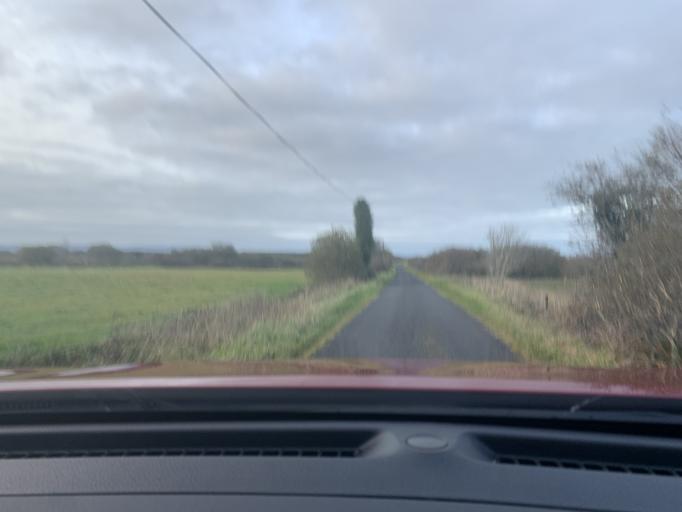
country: IE
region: Connaught
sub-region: Roscommon
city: Ballaghaderreen
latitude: 53.9574
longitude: -8.6022
